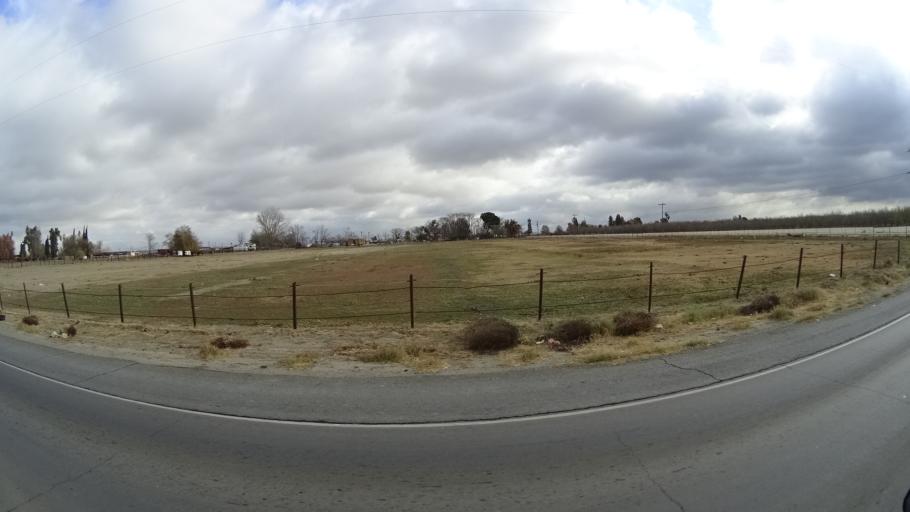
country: US
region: California
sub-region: Kern County
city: Greenfield
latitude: 35.2929
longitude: -118.9854
